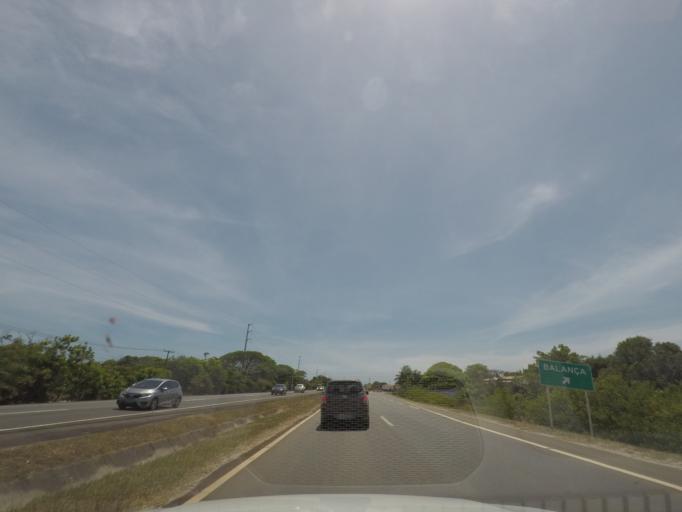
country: BR
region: Bahia
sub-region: Mata De Sao Joao
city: Mata de Sao Joao
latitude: -12.6259
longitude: -38.0622
